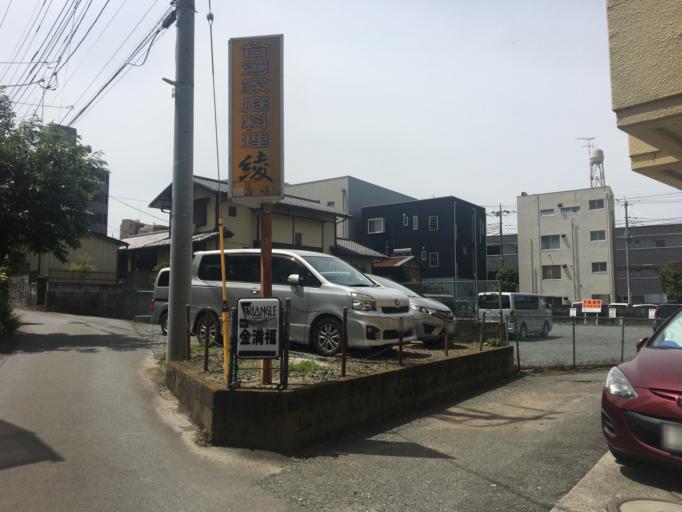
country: JP
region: Saitama
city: Sayama
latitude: 35.8552
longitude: 139.4152
